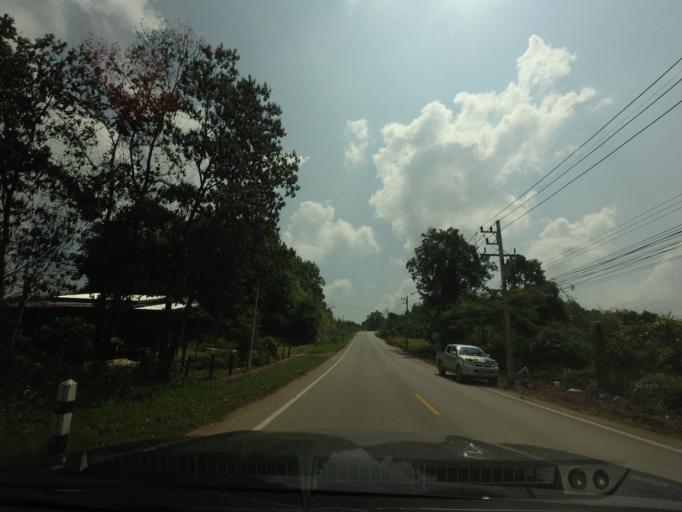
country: TH
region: Nan
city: Santi Suk
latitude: 18.9159
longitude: 100.8796
